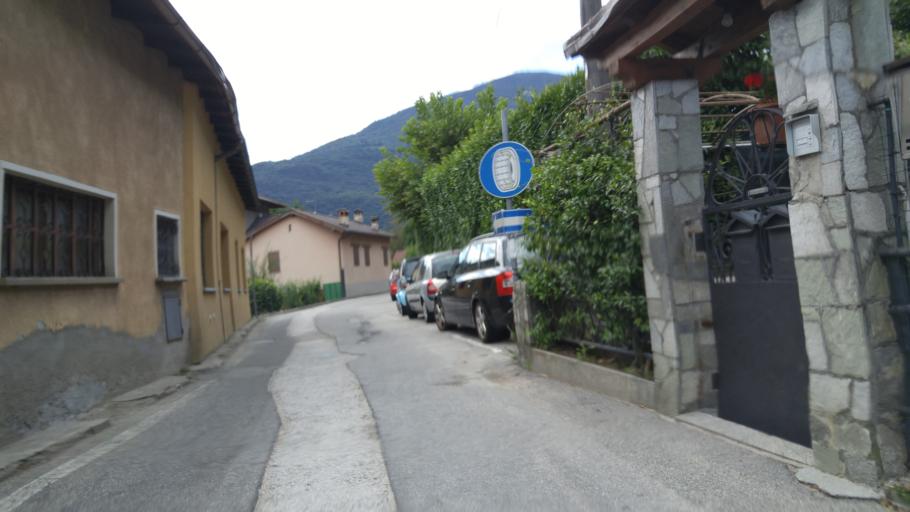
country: IT
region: Piedmont
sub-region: Provincia Verbano-Cusio-Ossola
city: Cannobio
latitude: 46.0706
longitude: 8.6935
